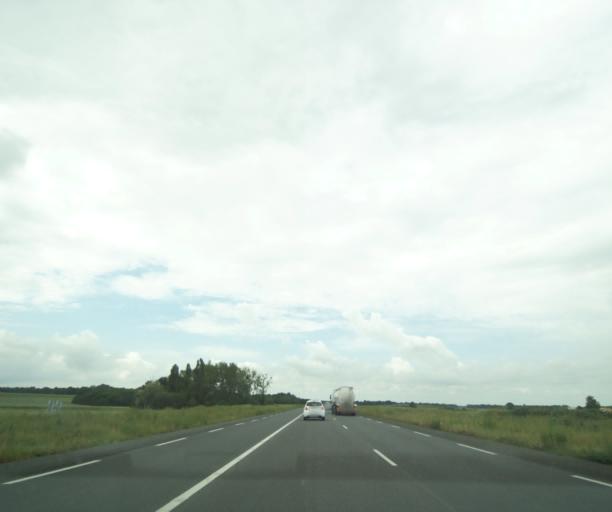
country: FR
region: Poitou-Charentes
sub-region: Departement des Deux-Sevres
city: Sainte-Verge
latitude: 47.0198
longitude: -0.2015
